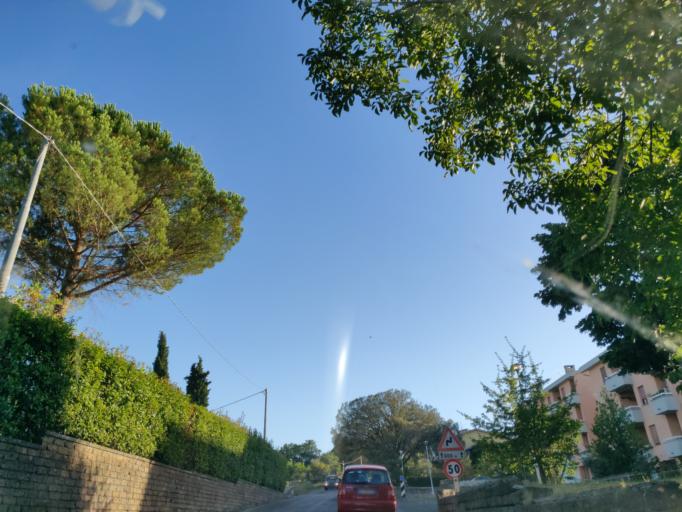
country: IT
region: Latium
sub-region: Provincia di Viterbo
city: Acquapendente
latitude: 42.7402
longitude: 11.8793
